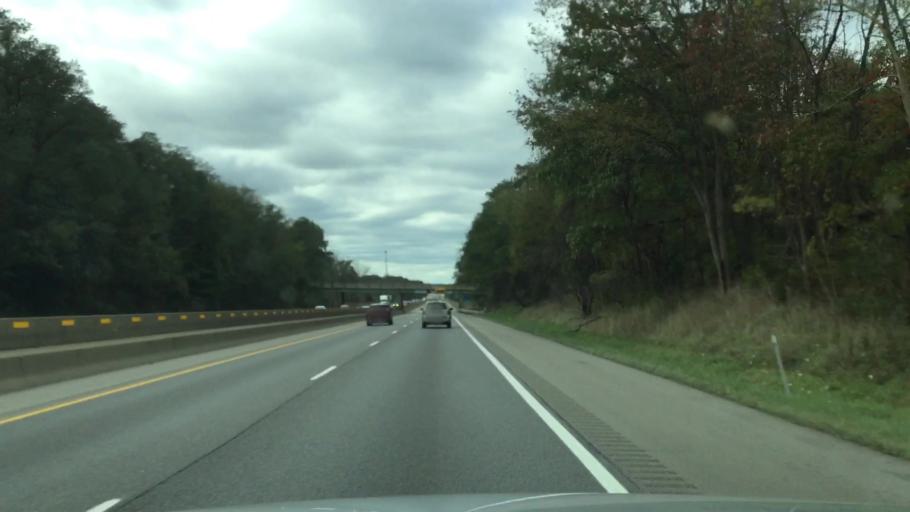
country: US
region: Michigan
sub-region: Kalamazoo County
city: Galesburg
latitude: 42.2794
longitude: -85.3979
